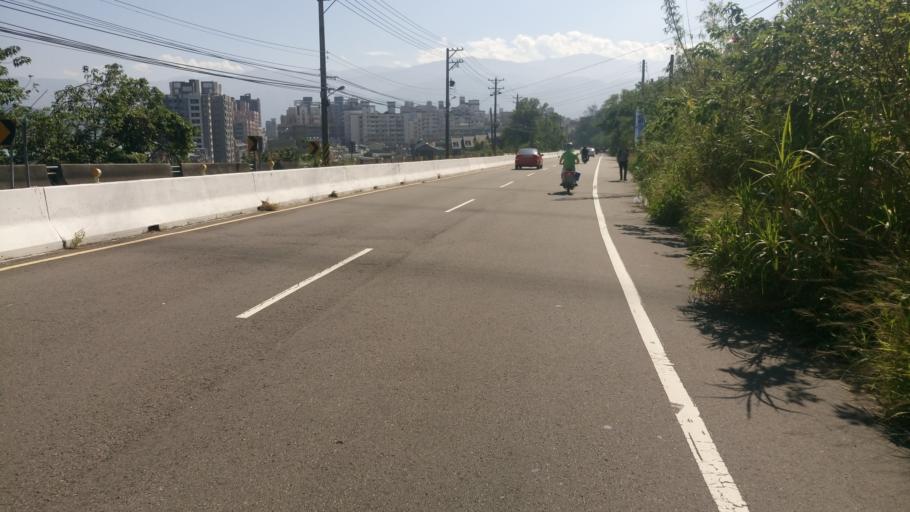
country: TW
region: Taiwan
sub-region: Hsinchu
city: Zhubei
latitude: 24.7515
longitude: 121.0774
